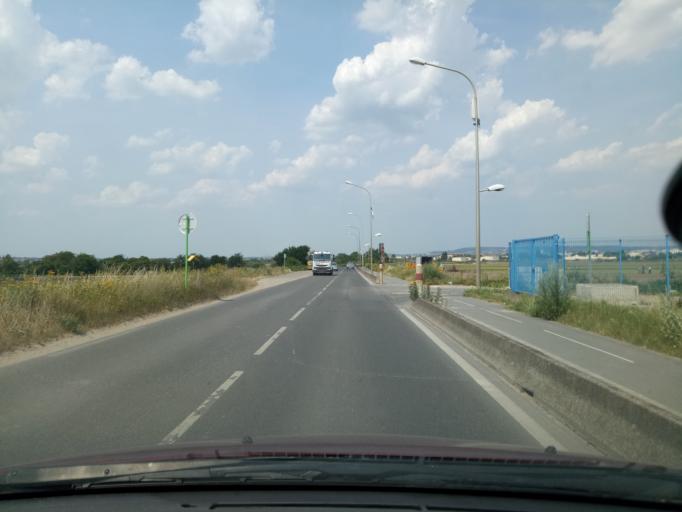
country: FR
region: Ile-de-France
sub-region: Departement des Yvelines
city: Montesson
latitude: 48.9160
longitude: 2.1526
